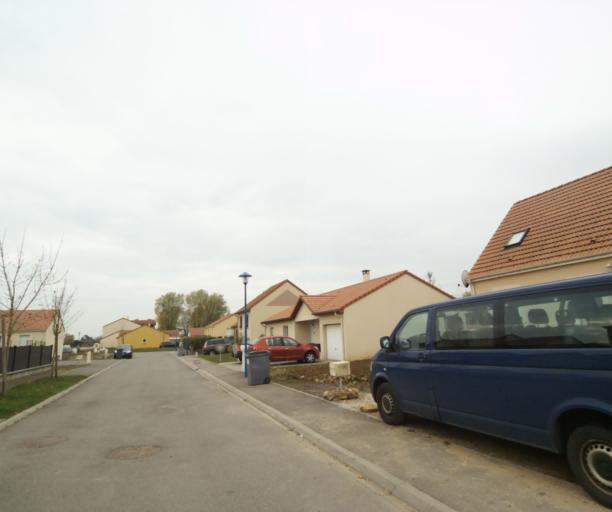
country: FR
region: Lorraine
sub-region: Departement de Meurthe-et-Moselle
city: Mancieulles
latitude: 49.2874
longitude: 5.8947
